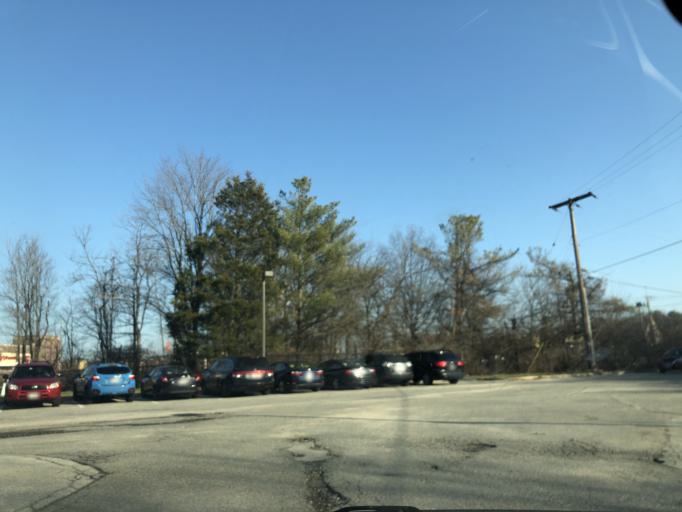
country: US
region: Maryland
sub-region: Montgomery County
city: Burtonsville
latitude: 39.1109
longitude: -76.9360
